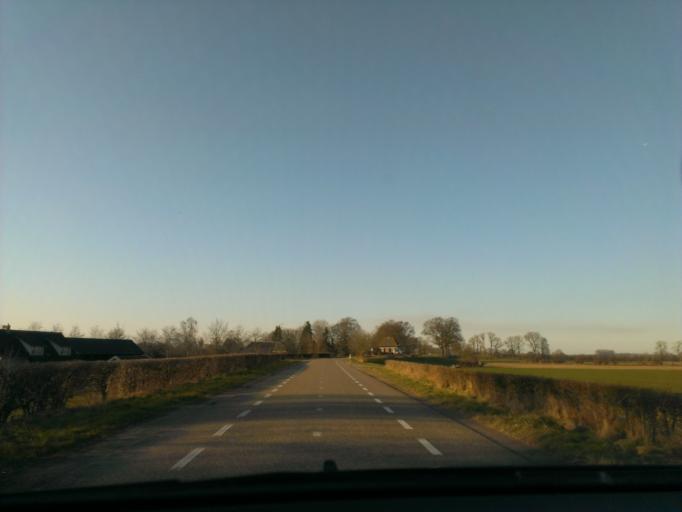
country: NL
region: Overijssel
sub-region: Gemeente Olst-Wijhe
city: Olst
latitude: 52.3046
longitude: 6.0917
